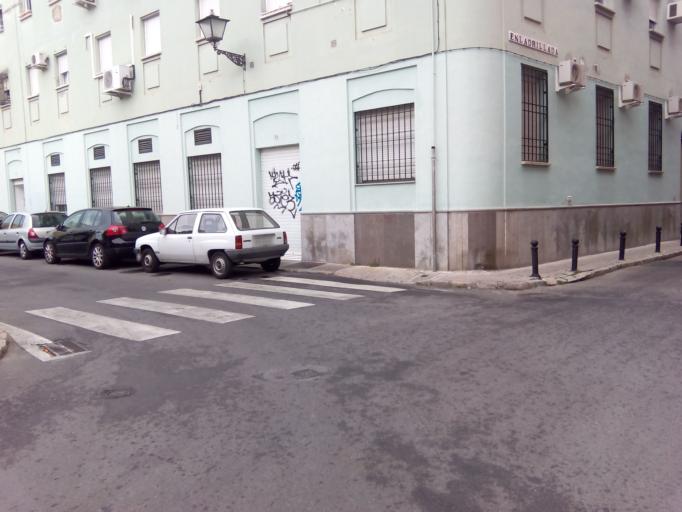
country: ES
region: Andalusia
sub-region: Provincia de Sevilla
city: Sevilla
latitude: 37.3976
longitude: -5.9839
